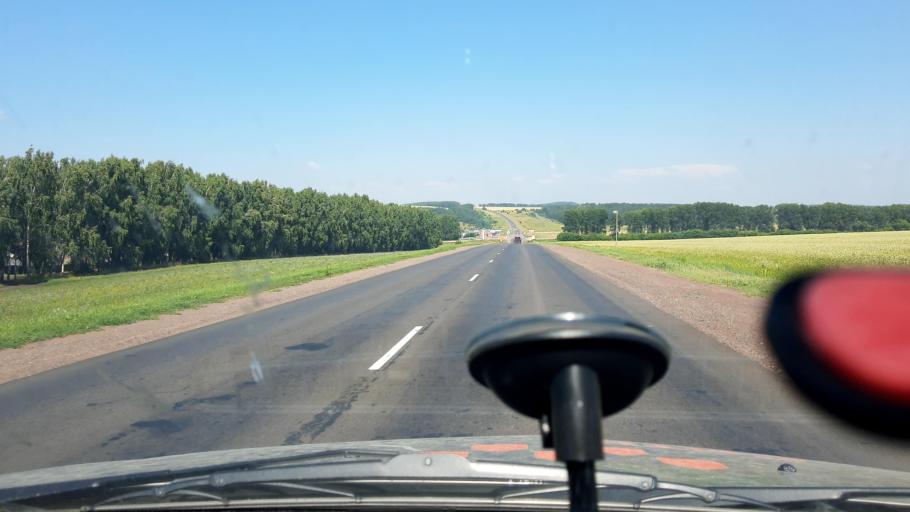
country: RU
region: Bashkortostan
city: Chekmagush
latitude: 55.1261
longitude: 54.6776
